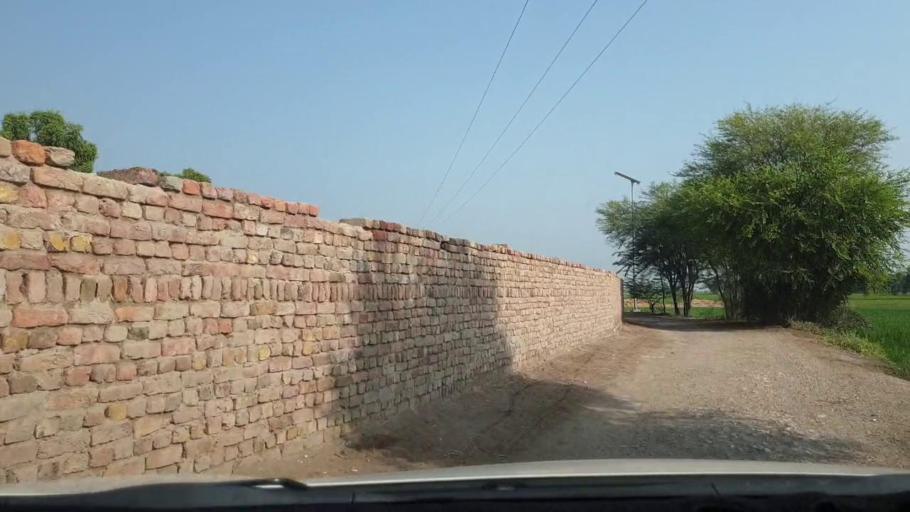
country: PK
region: Sindh
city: Goth Garelo
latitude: 27.4857
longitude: 68.1153
